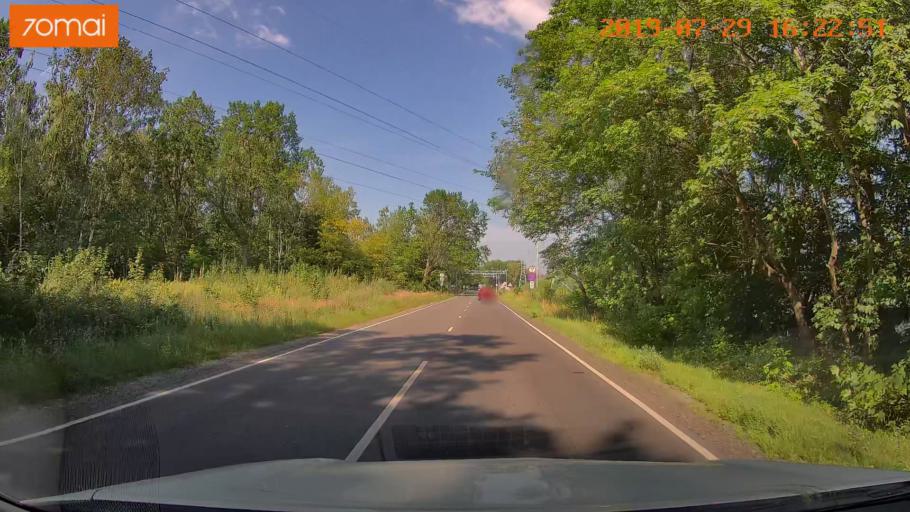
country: RU
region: Kaliningrad
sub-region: Gorod Kaliningrad
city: Baltiysk
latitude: 54.7015
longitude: 19.9421
